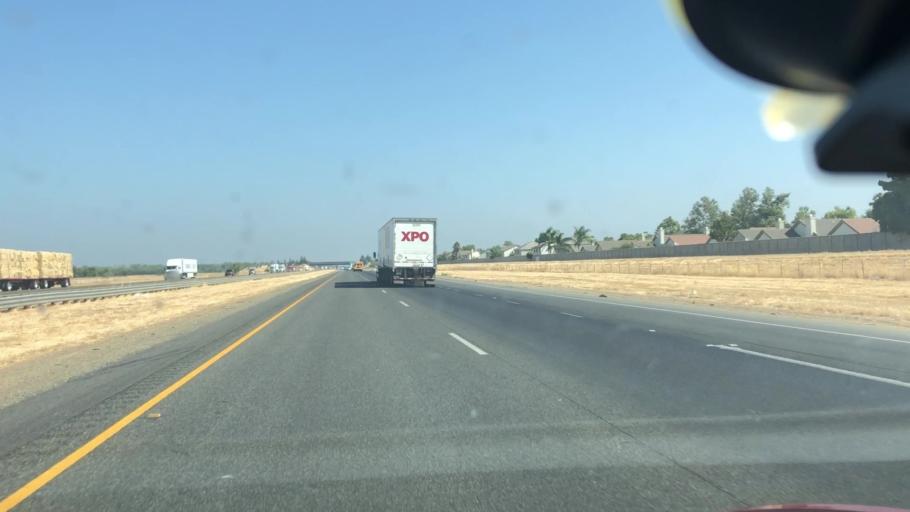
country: US
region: California
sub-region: Sacramento County
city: Laguna
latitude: 38.4157
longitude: -121.4850
